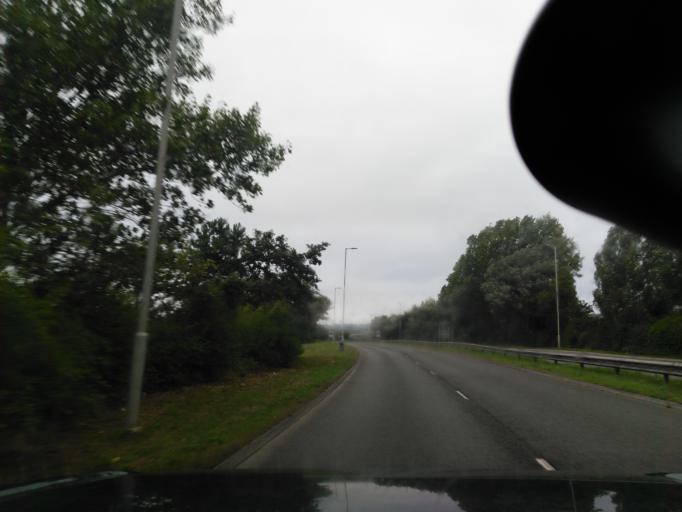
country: GB
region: England
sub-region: Poole
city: Poole
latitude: 50.7335
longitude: -1.9919
